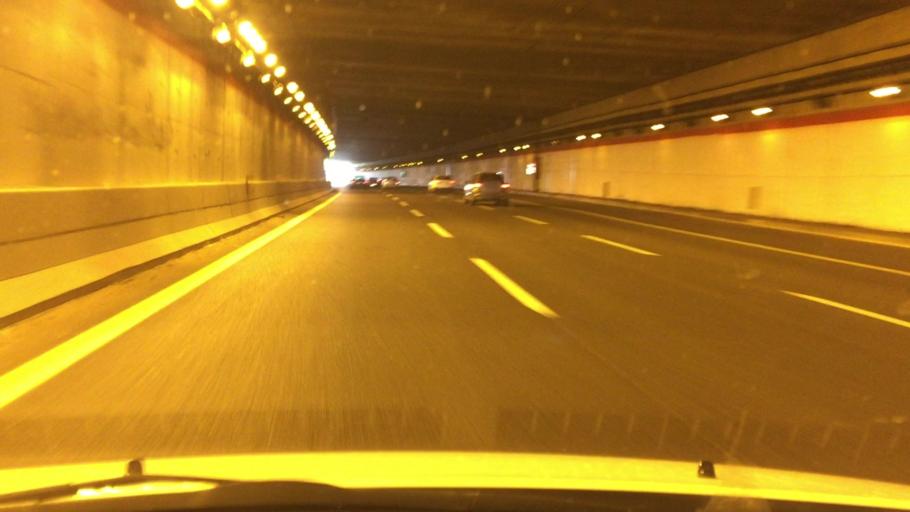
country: VA
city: Vatican City
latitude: 41.9815
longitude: 12.4514
